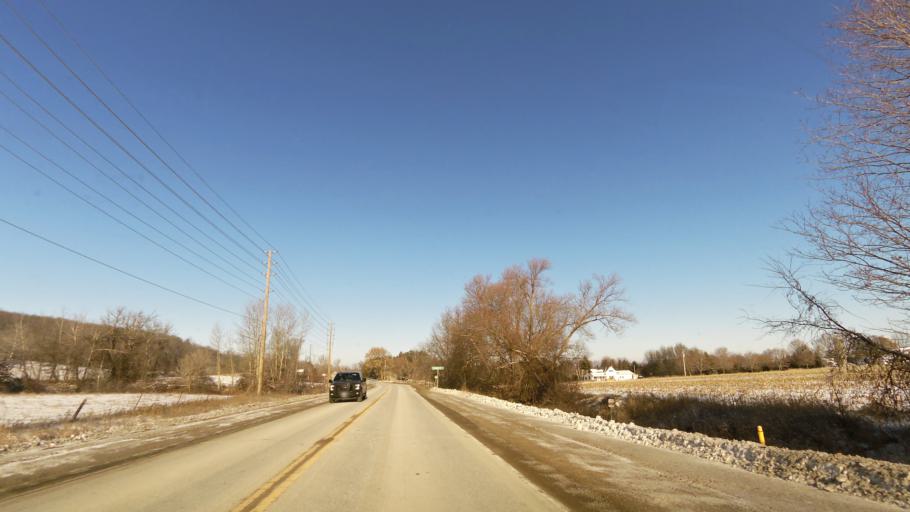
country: CA
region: Ontario
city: Quinte West
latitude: 44.1862
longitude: -77.8116
